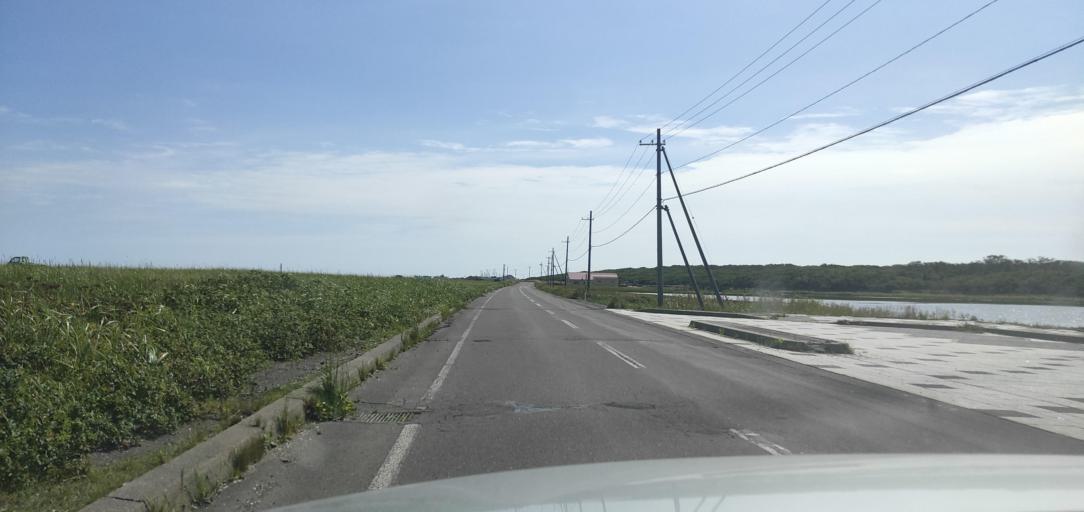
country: JP
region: Hokkaido
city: Shibetsu
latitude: 43.6092
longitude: 145.2745
